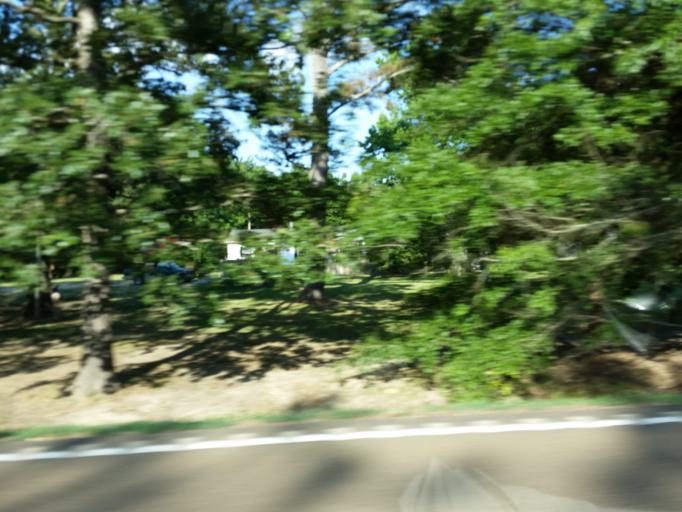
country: US
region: Mississippi
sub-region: Calhoun County
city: Calhoun City
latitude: 33.7675
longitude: -89.3639
